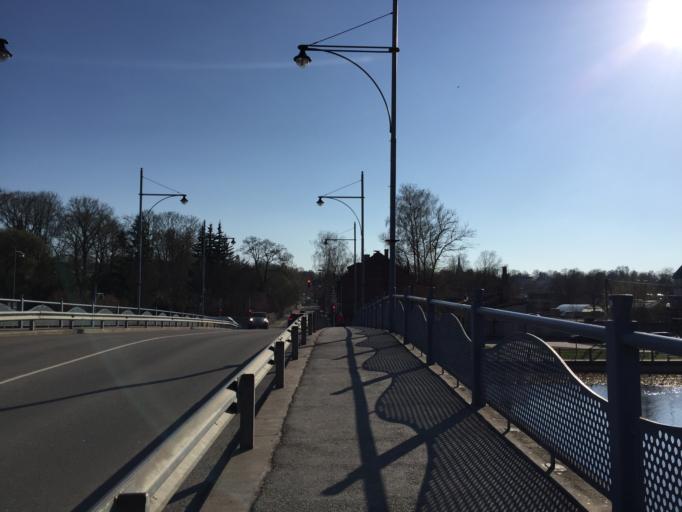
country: EE
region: Tartu
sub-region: Tartu linn
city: Tartu
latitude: 58.3866
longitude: 26.7222
